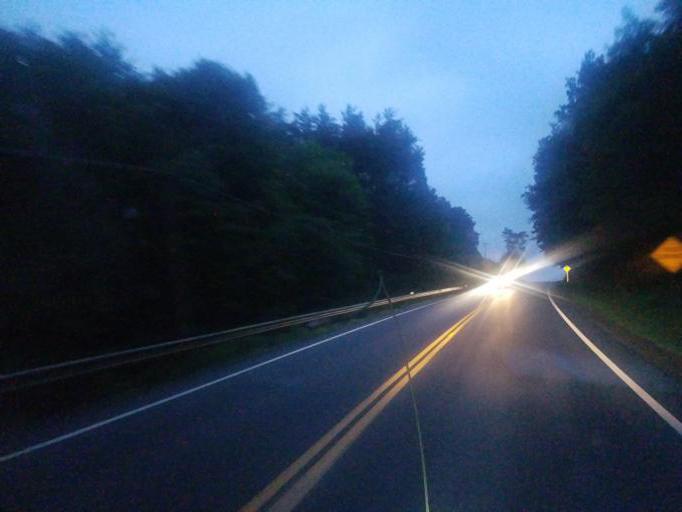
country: US
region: Ohio
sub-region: Carroll County
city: Carrollton
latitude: 40.5577
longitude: -81.0568
